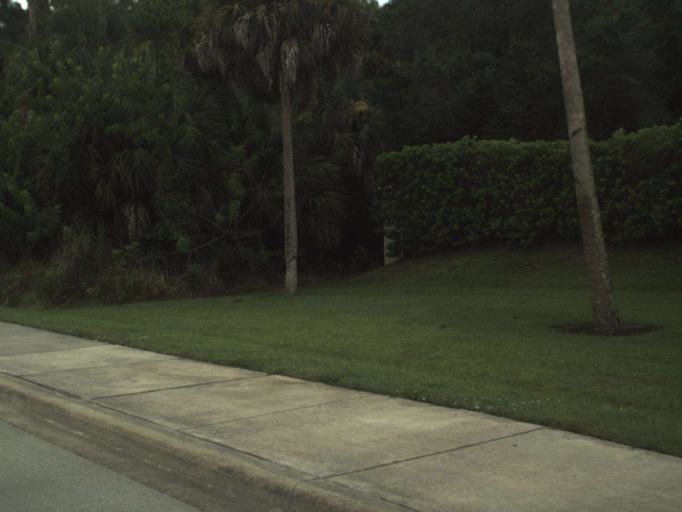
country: US
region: Florida
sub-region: Saint Lucie County
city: Fort Pierce South
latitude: 27.4016
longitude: -80.3500
